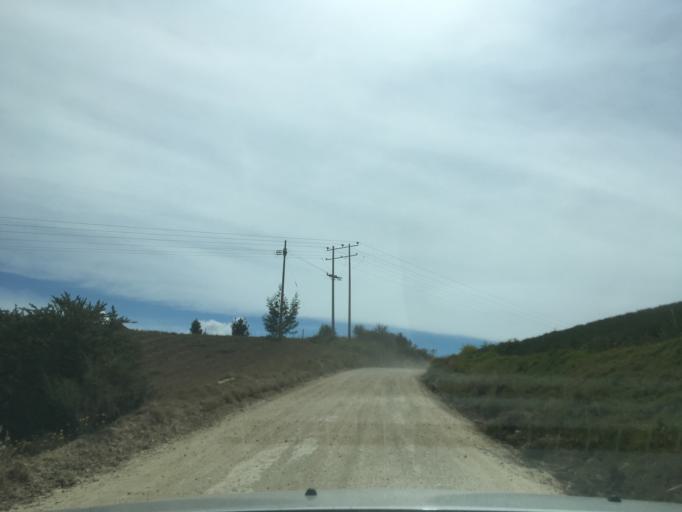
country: CO
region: Boyaca
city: Aquitania
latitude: 5.5945
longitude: -72.9183
